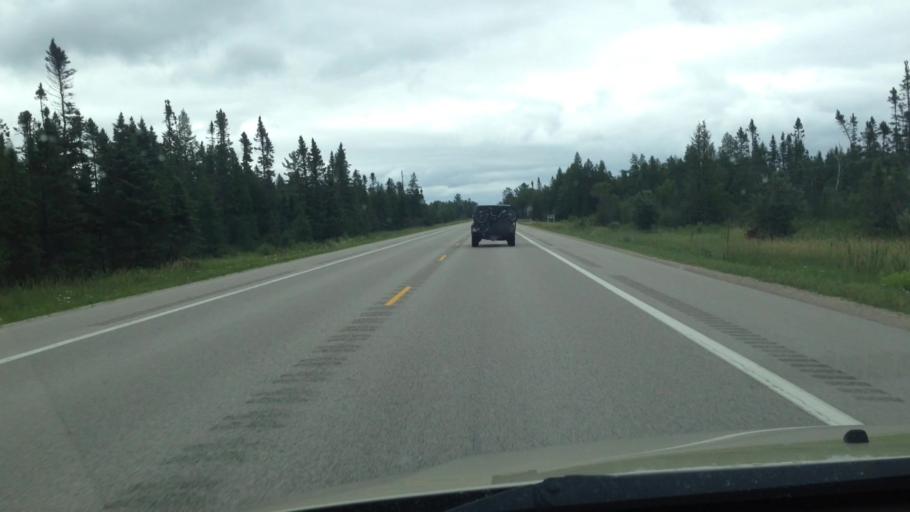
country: US
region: Michigan
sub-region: Luce County
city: Newberry
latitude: 46.1007
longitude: -85.5328
